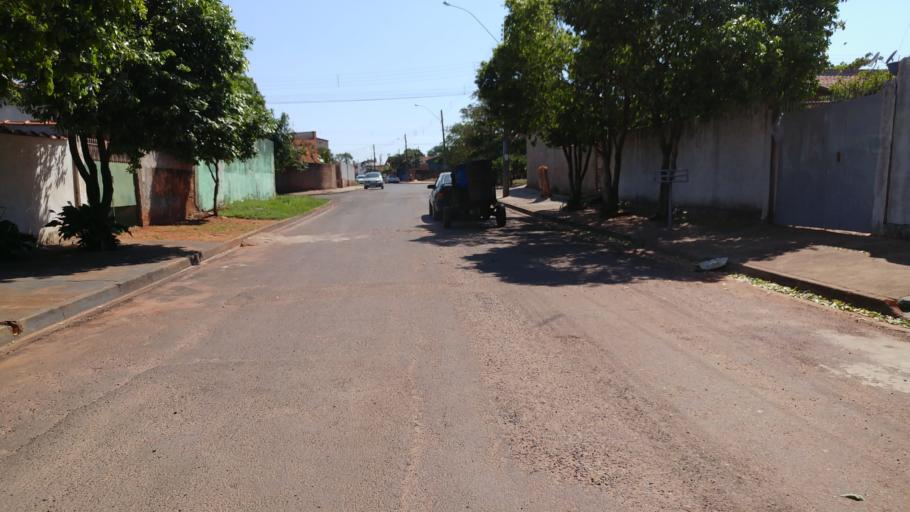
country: BR
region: Sao Paulo
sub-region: Paraguacu Paulista
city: Paraguacu Paulista
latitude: -22.4210
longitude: -50.5888
